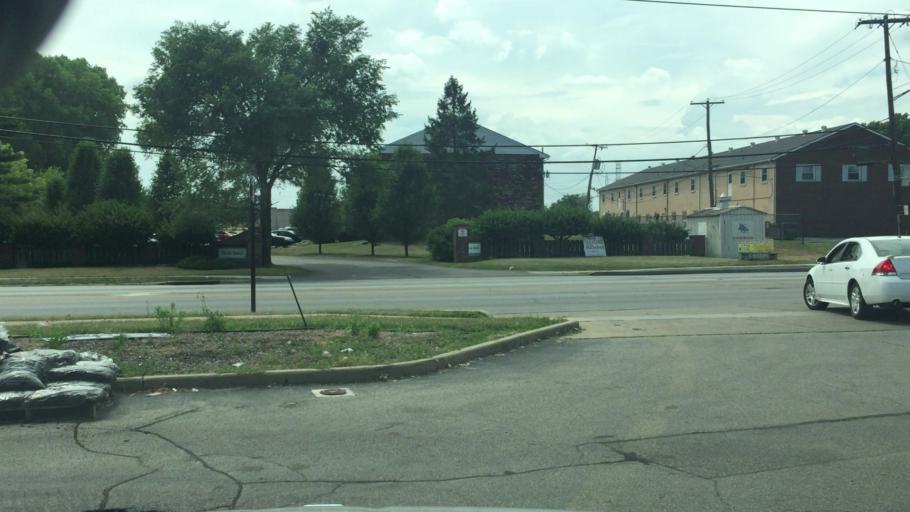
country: US
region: Ohio
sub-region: Lucas County
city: Oregon
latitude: 41.7085
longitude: -83.4990
